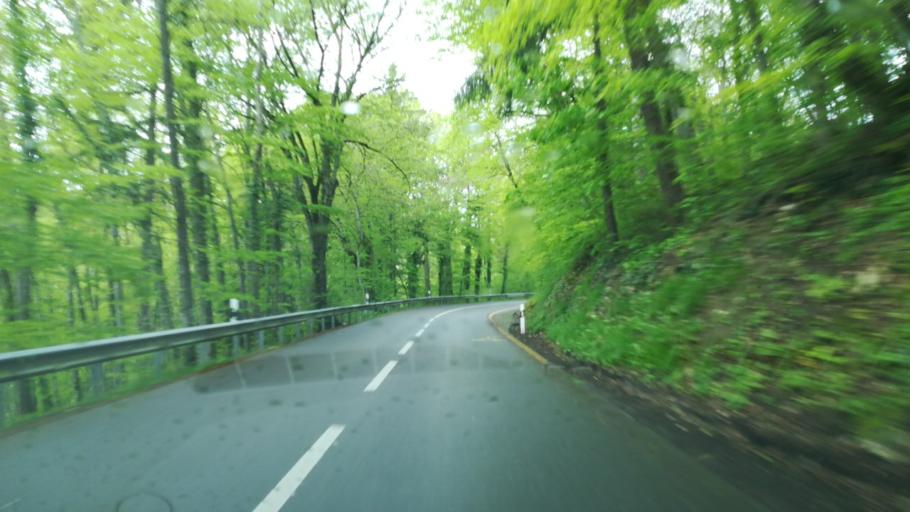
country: CH
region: Schaffhausen
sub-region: Bezirk Reiat
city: Stetten
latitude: 47.7530
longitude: 8.6612
